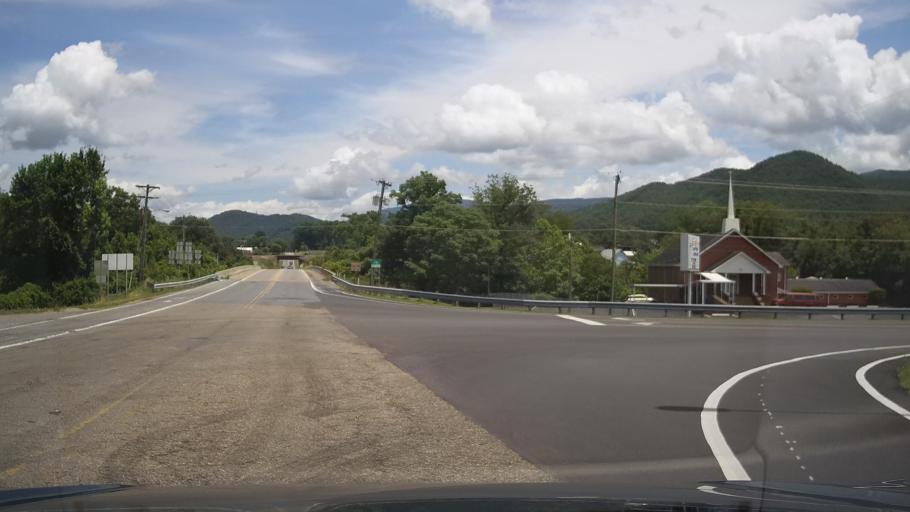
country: US
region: Tennessee
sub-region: Unicoi County
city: Banner Hill
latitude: 36.1230
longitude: -82.4450
